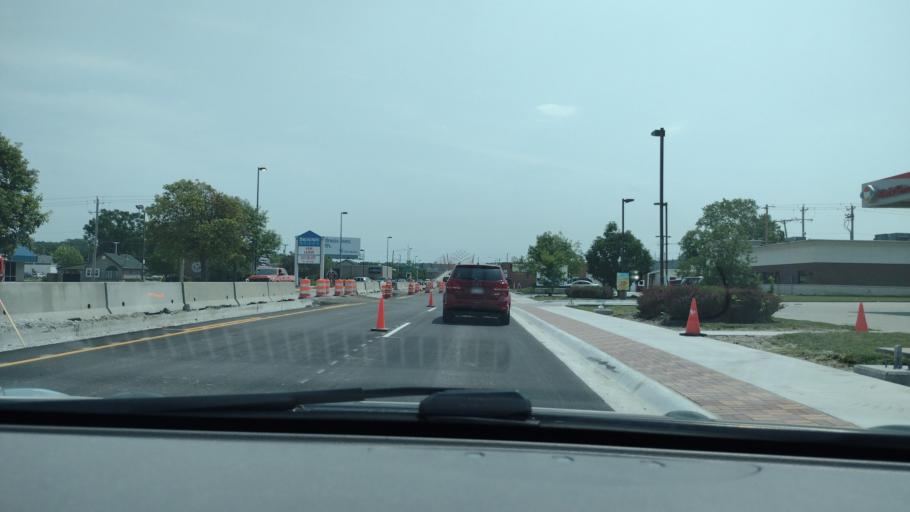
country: US
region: Iowa
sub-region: Pottawattamie County
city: Council Bluffs
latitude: 41.2618
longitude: -95.8704
